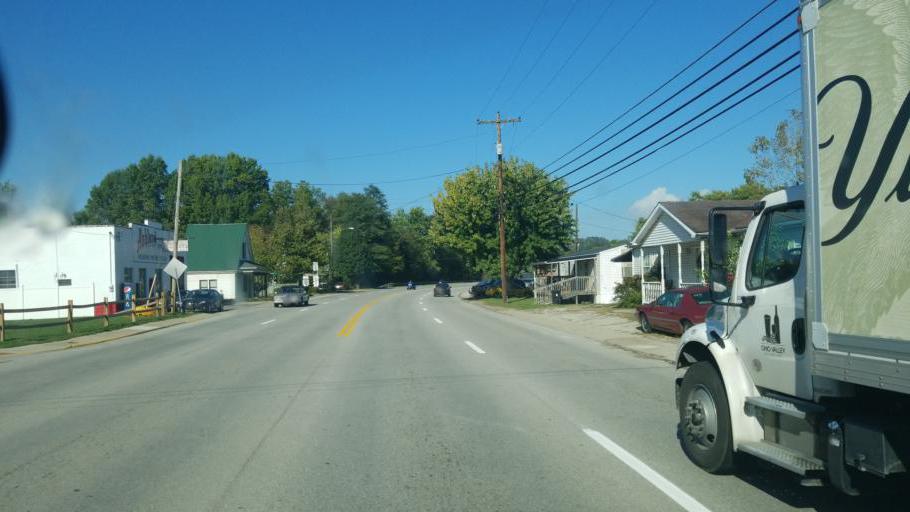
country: US
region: Ohio
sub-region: Brown County
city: Aberdeen
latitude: 38.6559
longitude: -83.7625
